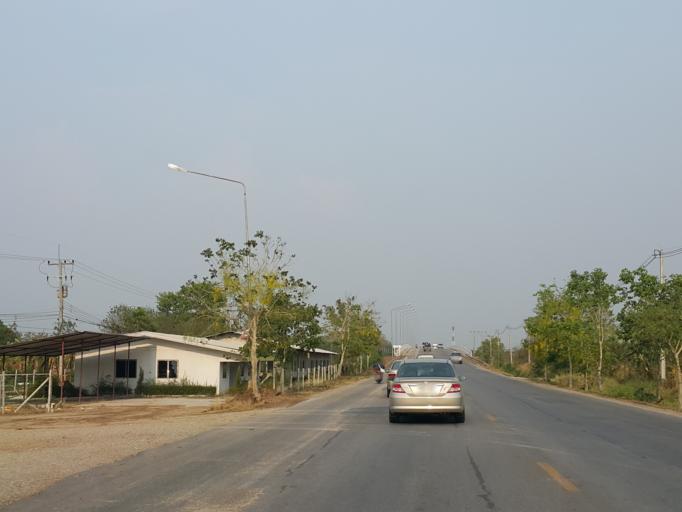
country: TH
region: Chiang Mai
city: San Sai
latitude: 18.8667
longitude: 98.9733
